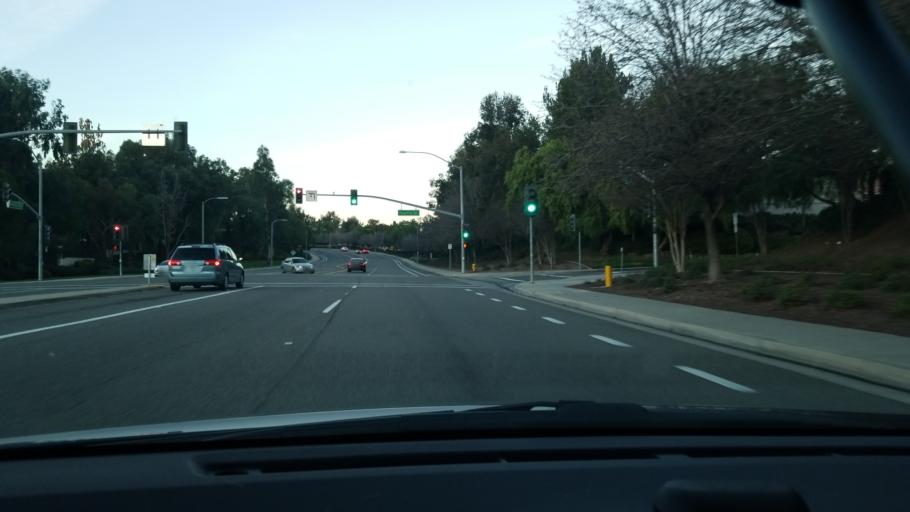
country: US
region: California
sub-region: Riverside County
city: Temecula
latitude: 33.5098
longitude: -117.1242
